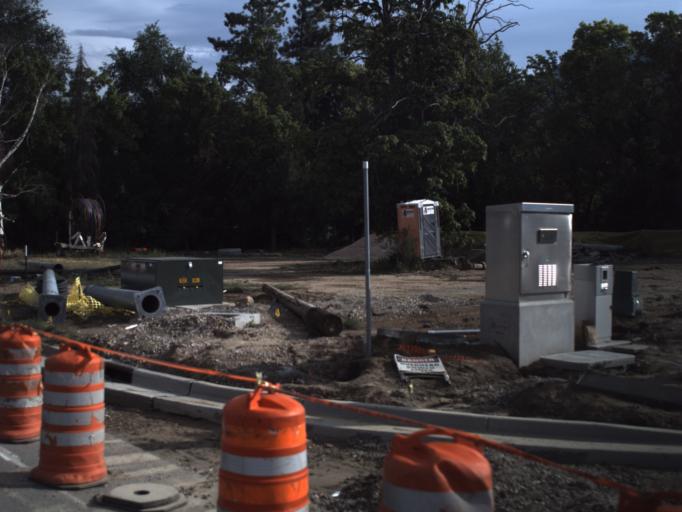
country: US
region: Utah
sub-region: Weber County
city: Harrisville
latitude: 41.2667
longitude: -111.9694
